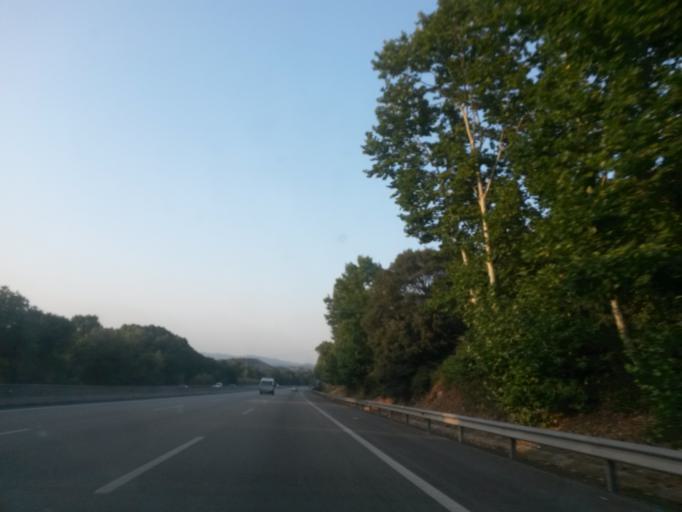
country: ES
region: Catalonia
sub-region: Provincia de Barcelona
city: Sant Celoni
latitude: 41.6965
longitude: 2.5138
